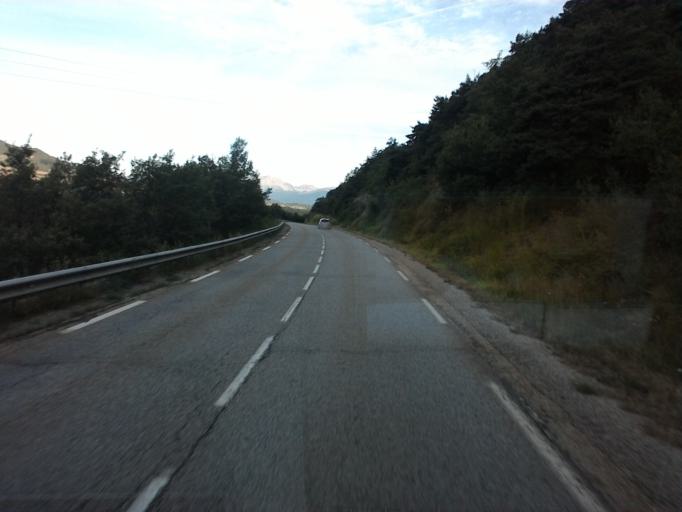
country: FR
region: Rhone-Alpes
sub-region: Departement de l'Isere
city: La Mure
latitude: 44.8443
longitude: 5.8683
